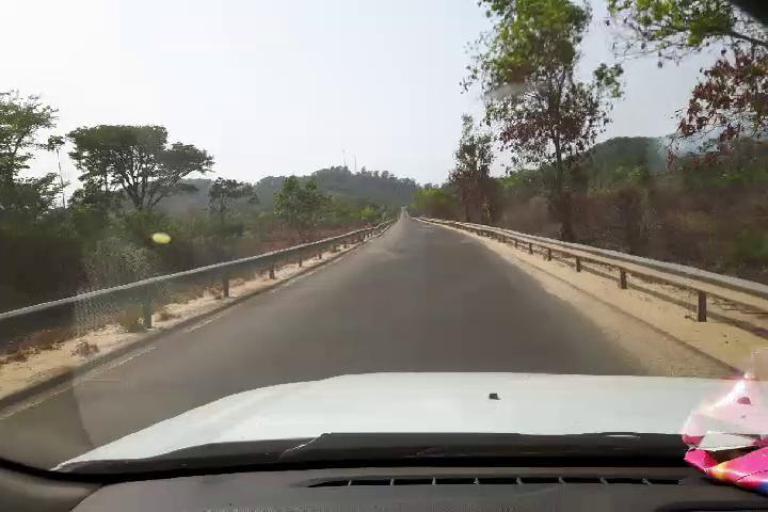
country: SL
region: Western Area
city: Waterloo
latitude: 8.2558
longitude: -13.1576
